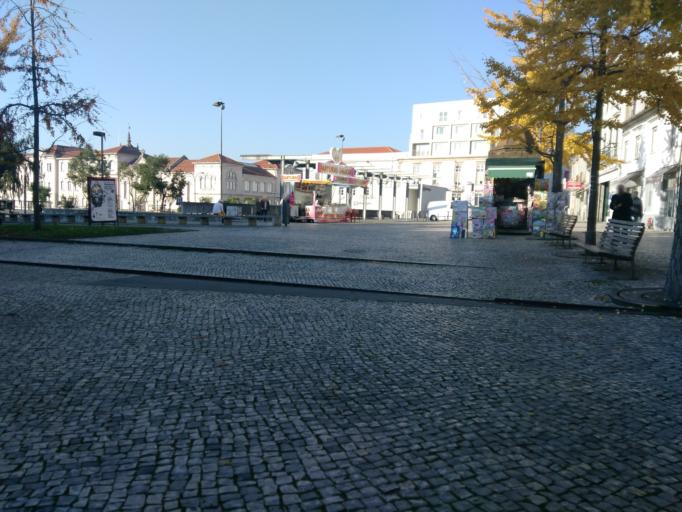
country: PT
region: Braga
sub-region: Braga
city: Braga
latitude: 41.5521
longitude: -8.4255
